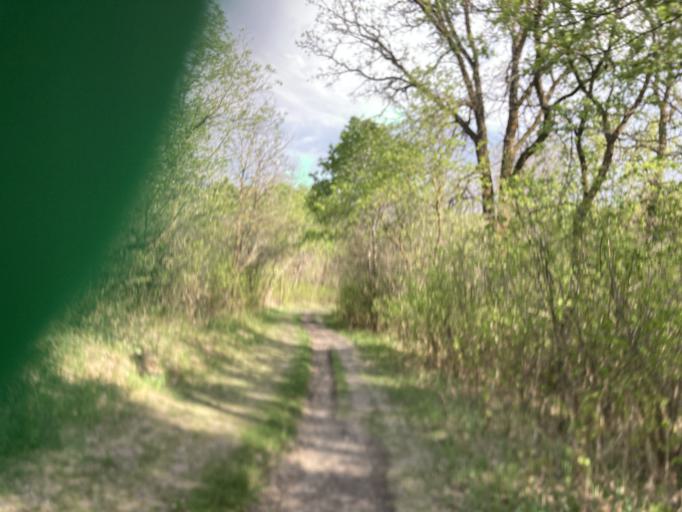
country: CA
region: Manitoba
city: Brandon
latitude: 49.7221
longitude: -99.9081
